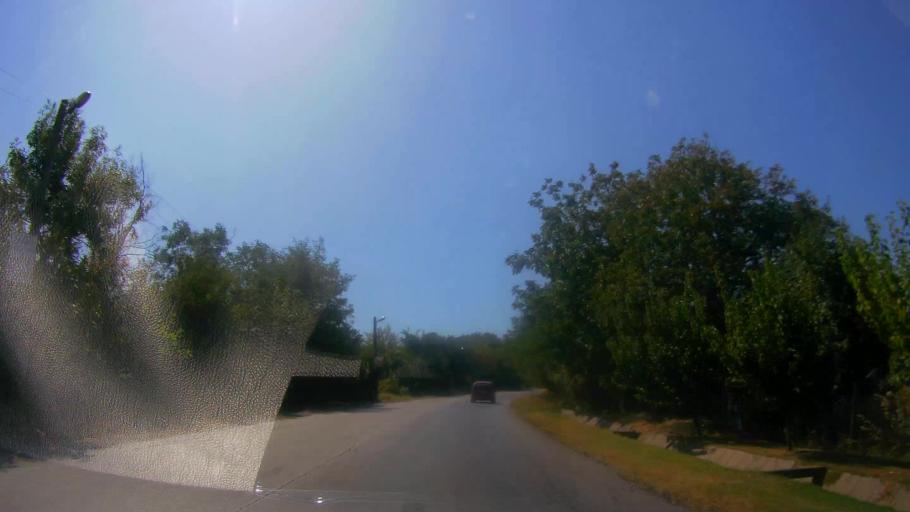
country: BG
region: Veliko Turnovo
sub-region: Obshtina Gorna Oryakhovitsa
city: Purvomaytsi
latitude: 43.1696
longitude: 25.6200
